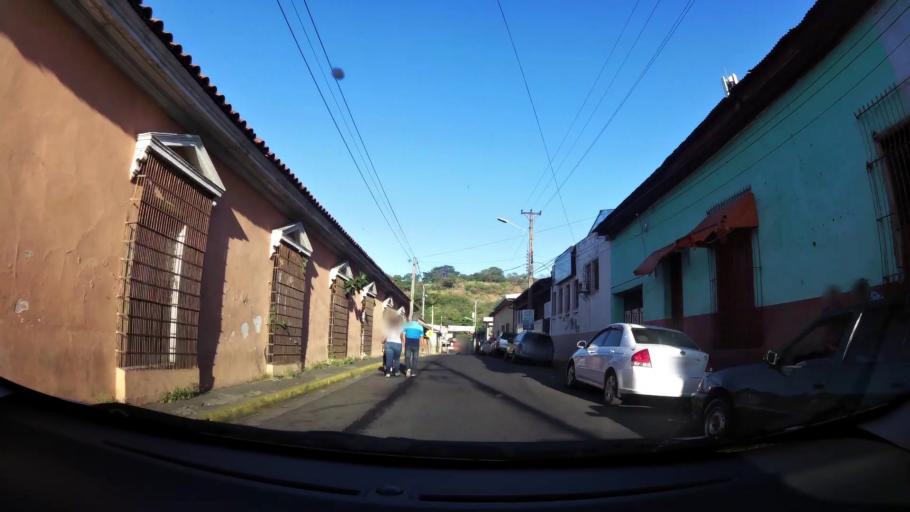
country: SV
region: Sonsonate
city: Sonsonate
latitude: 13.7231
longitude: -89.7291
